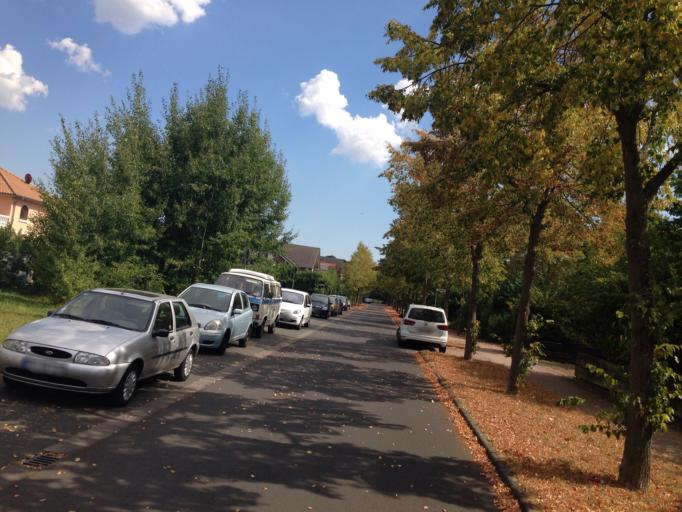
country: DE
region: Hesse
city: Allendorf an der Lahn
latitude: 50.5544
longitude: 8.6406
